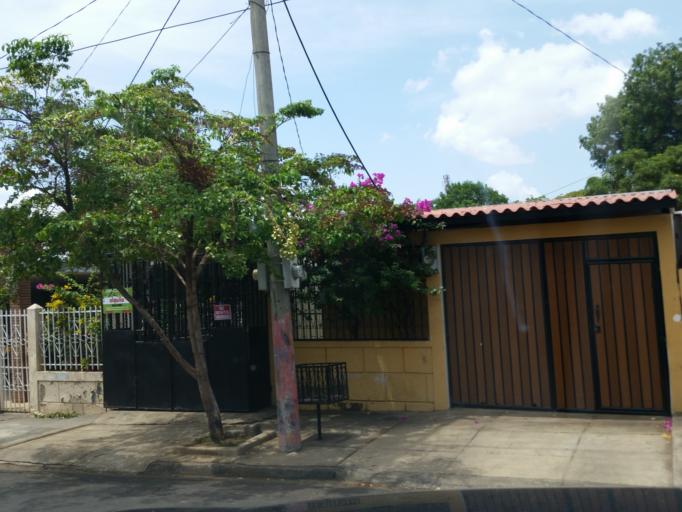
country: NI
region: Managua
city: Managua
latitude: 12.1209
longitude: -86.2486
